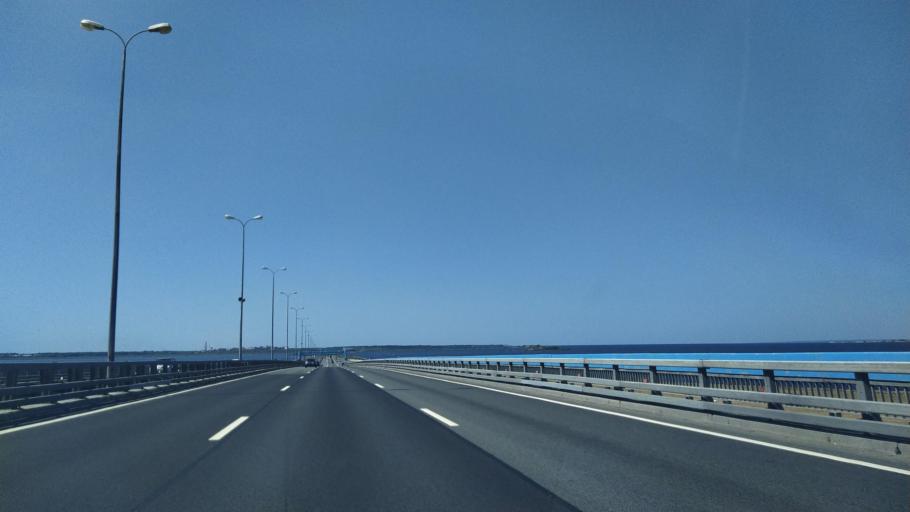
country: RU
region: St.-Petersburg
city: Kronshtadt
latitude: 60.0264
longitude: 29.8289
